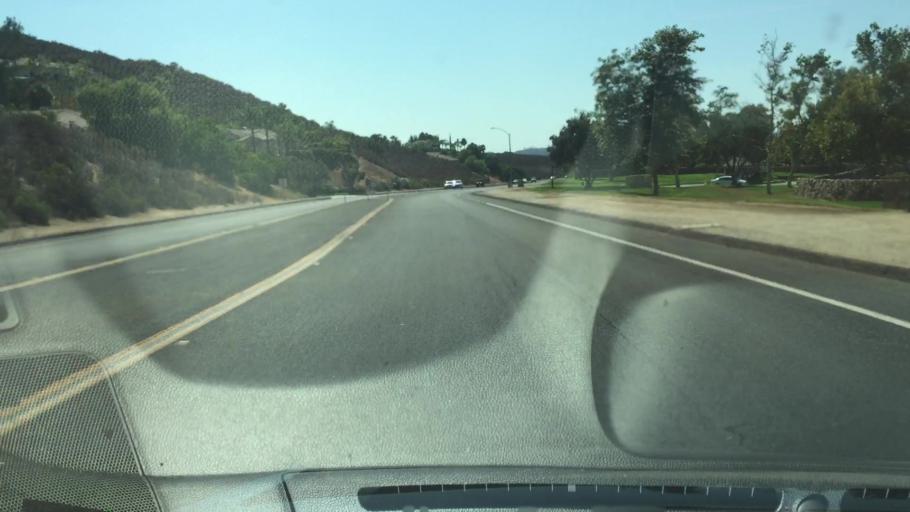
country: US
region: California
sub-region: San Diego County
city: Jamul
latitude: 32.7391
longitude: -116.8963
